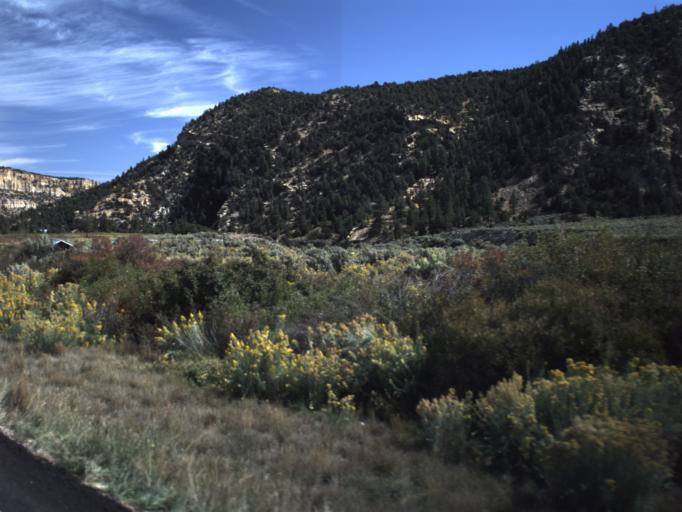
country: US
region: Utah
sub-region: Garfield County
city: Panguitch
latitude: 37.7148
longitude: -111.7854
